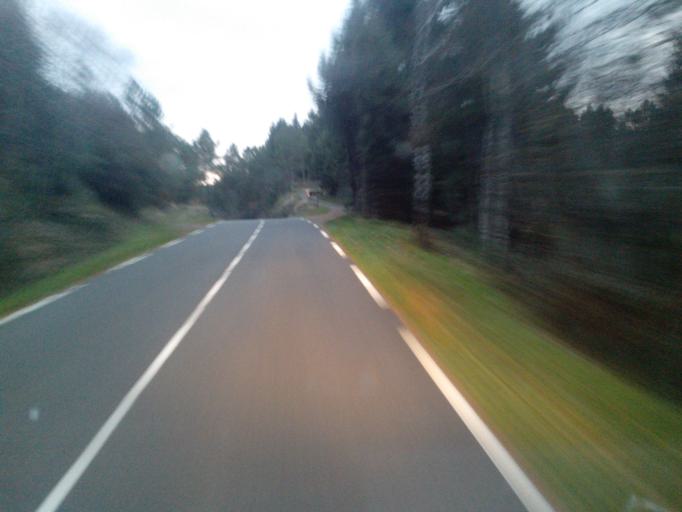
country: FR
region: Languedoc-Roussillon
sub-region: Departement du Gard
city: Saint-Jean-du-Gard
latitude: 44.1406
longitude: 3.7803
